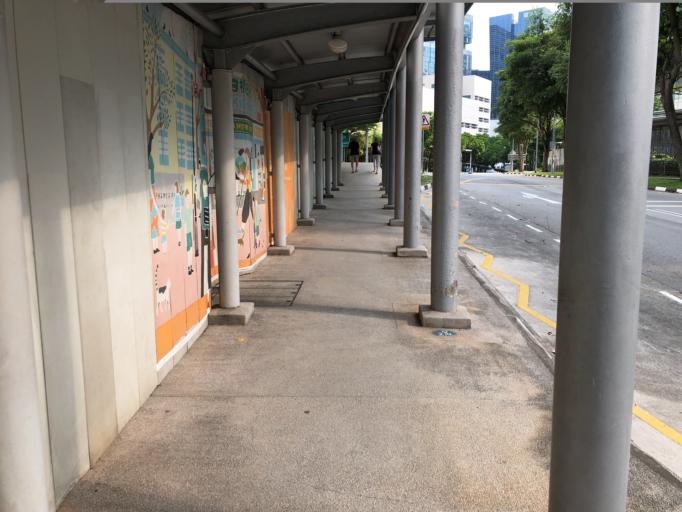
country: SG
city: Singapore
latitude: 1.3237
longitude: 103.8459
